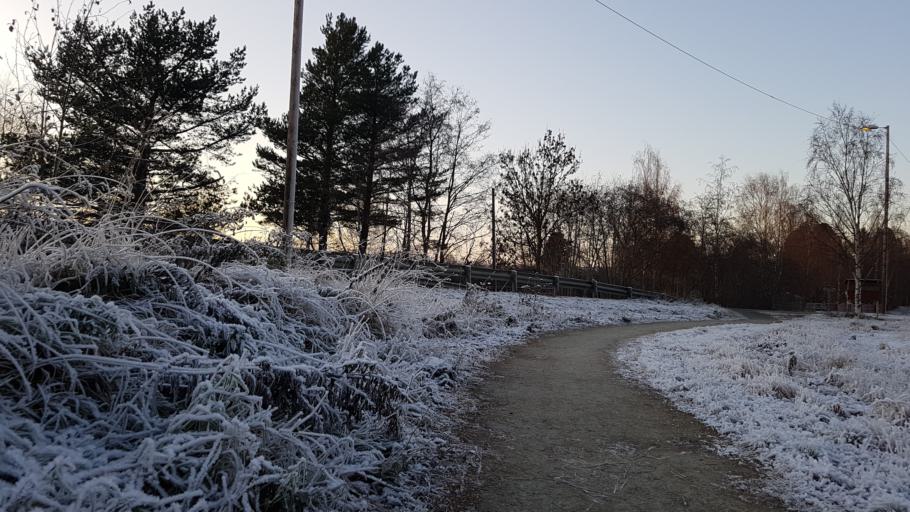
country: NO
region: Sor-Trondelag
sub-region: Melhus
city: Melhus
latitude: 63.2747
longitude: 10.2943
